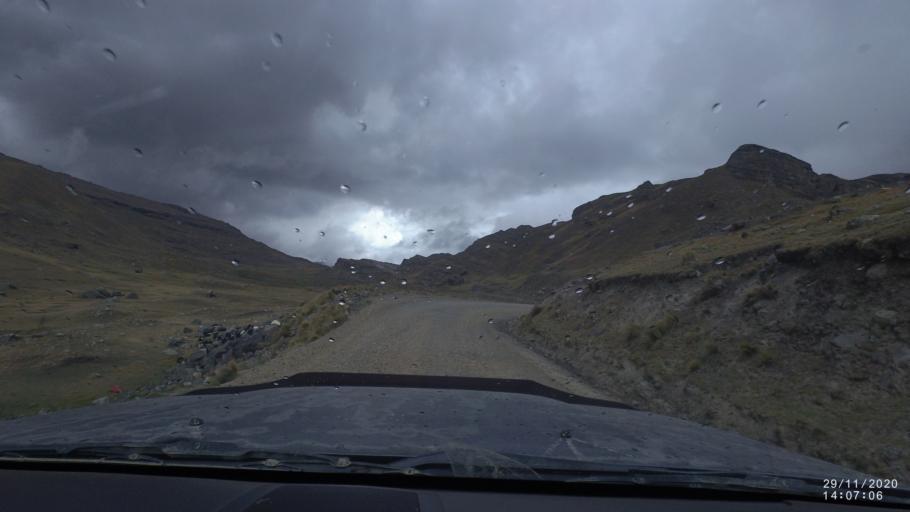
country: BO
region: Cochabamba
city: Sipe Sipe
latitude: -17.2179
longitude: -66.3816
